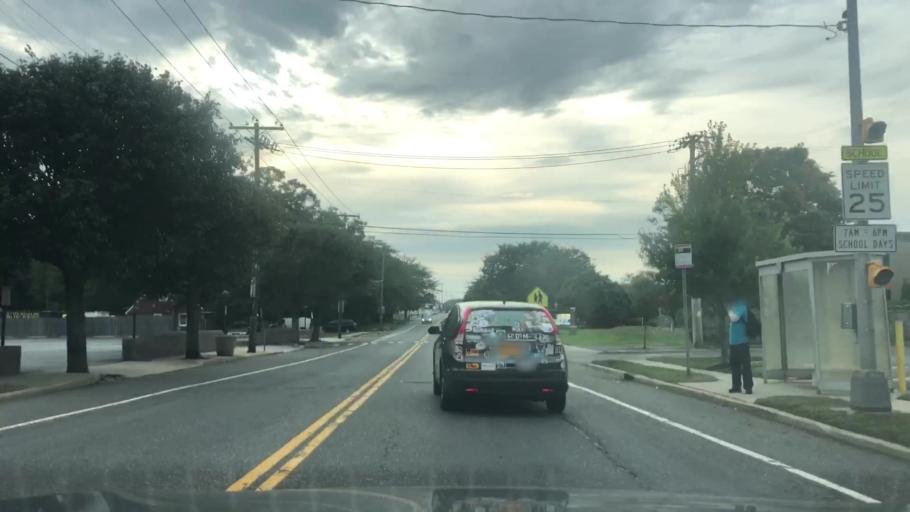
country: US
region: New York
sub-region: Nassau County
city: Massapequa
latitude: 40.6914
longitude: -73.4802
